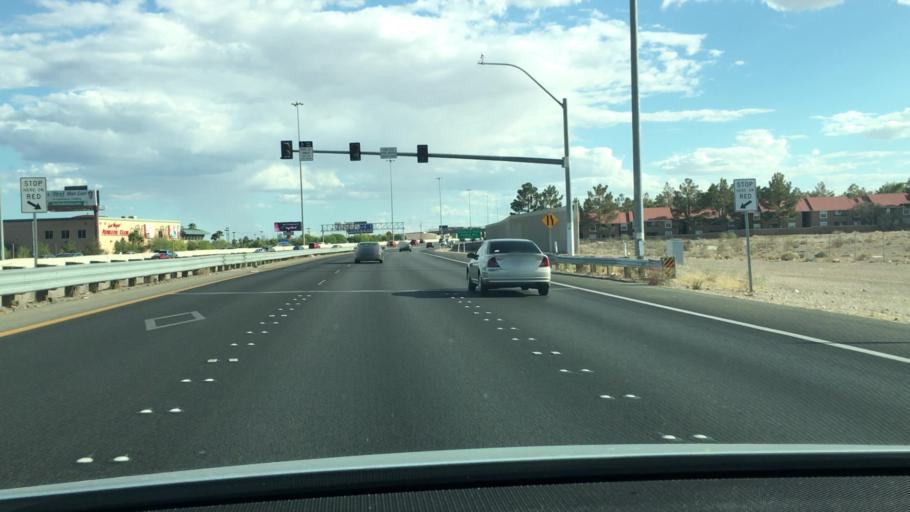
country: US
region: Nevada
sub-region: Clark County
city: Spring Valley
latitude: 36.1942
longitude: -115.2453
